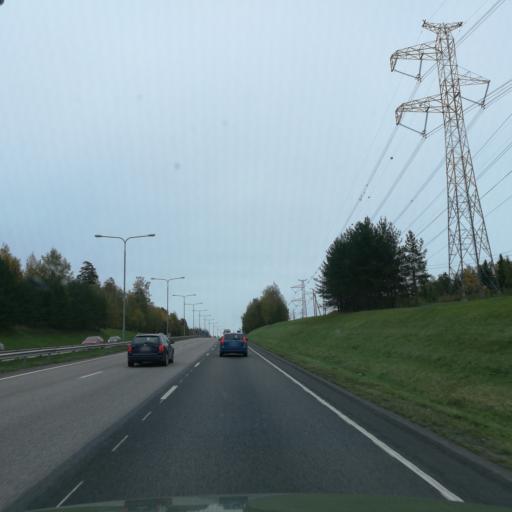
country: FI
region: Uusimaa
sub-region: Helsinki
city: Vantaa
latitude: 60.2793
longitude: 25.0598
